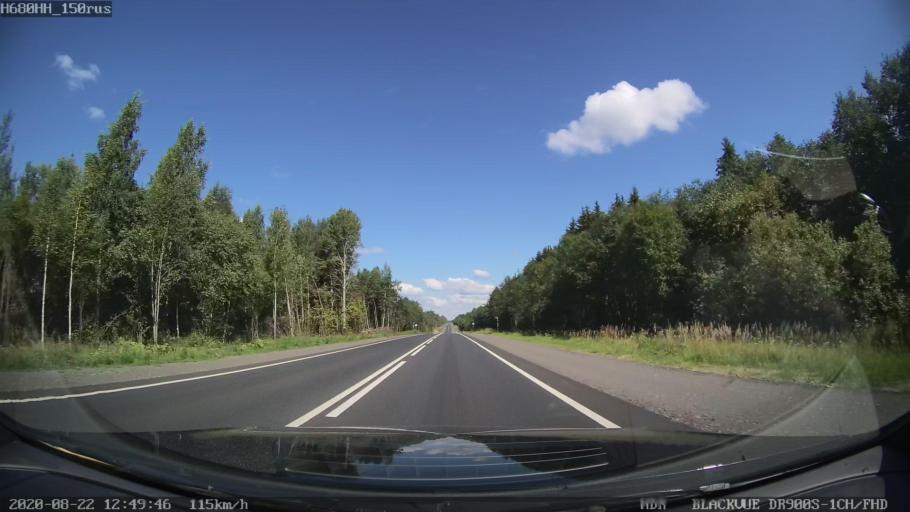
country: RU
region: Tverskaya
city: Rameshki
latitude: 57.4563
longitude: 36.2110
